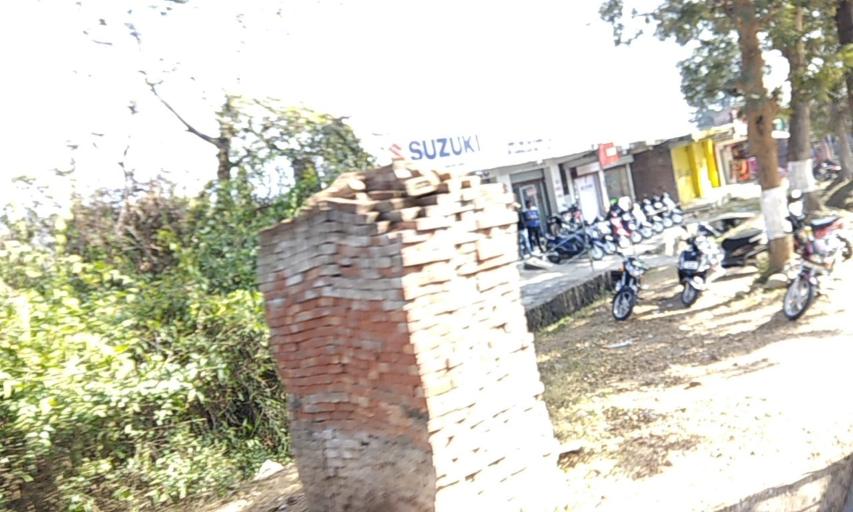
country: IN
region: Himachal Pradesh
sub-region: Kangra
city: Yol
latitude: 32.2178
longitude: 76.1784
